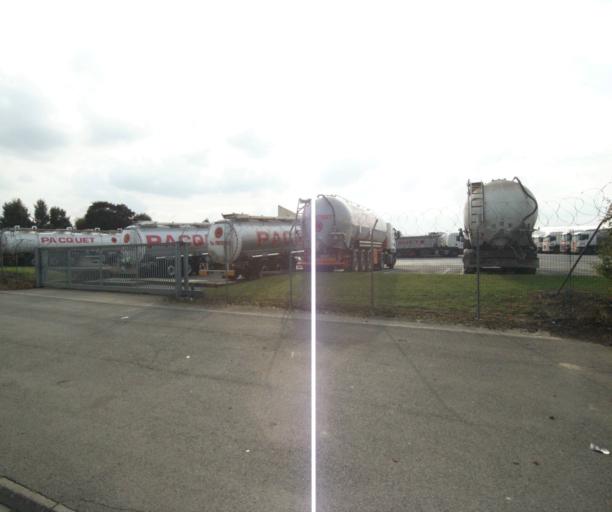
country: FR
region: Nord-Pas-de-Calais
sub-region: Departement du Nord
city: Santes
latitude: 50.6011
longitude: 2.9629
